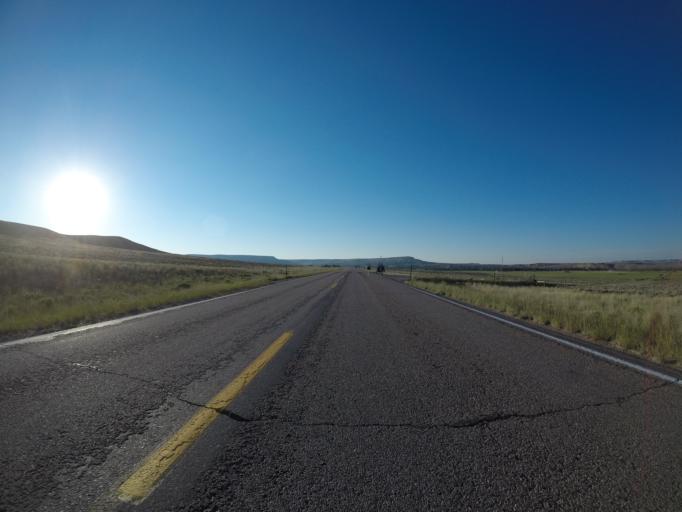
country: US
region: Wyoming
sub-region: Sublette County
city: Marbleton
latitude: 42.5739
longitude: -109.9784
